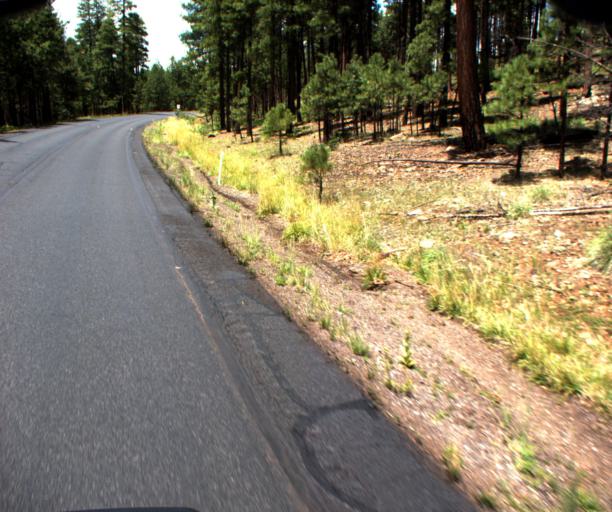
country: US
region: Arizona
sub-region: Gila County
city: Pine
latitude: 34.4603
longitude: -111.4409
